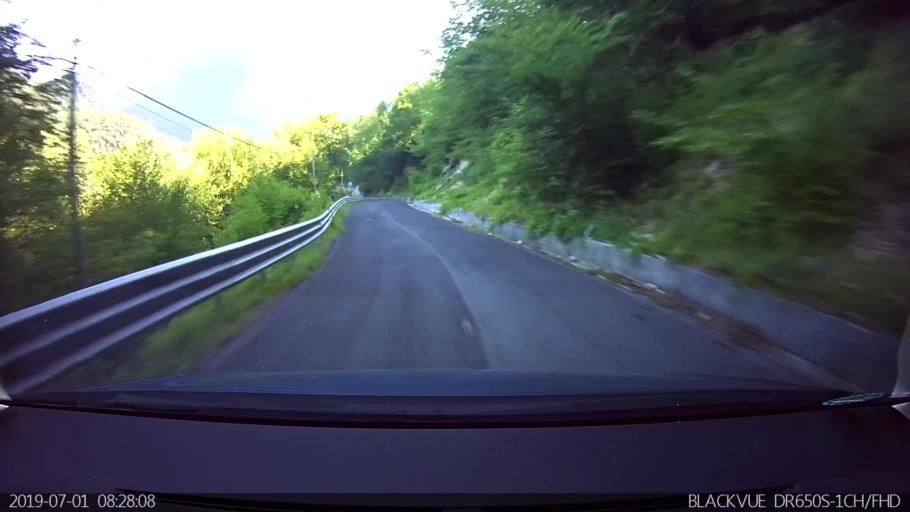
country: IT
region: Latium
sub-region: Provincia di Frosinone
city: Collepardo
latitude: 41.7763
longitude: 13.4080
